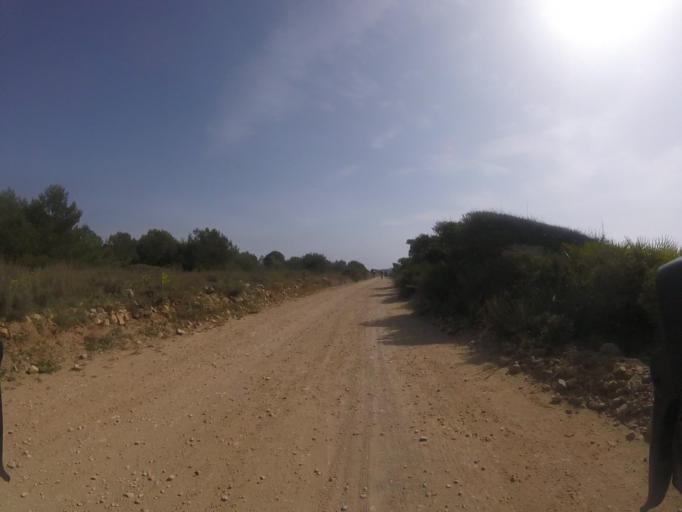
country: ES
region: Valencia
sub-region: Provincia de Castello
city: Alcoceber
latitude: 40.2943
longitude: 0.3389
